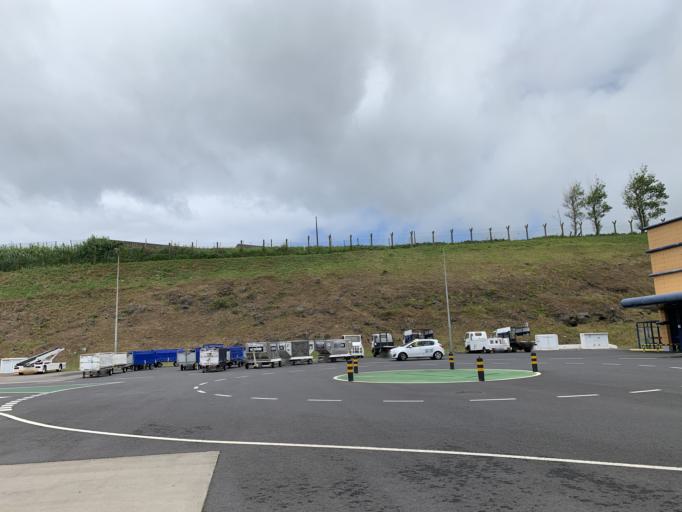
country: PT
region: Azores
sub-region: Ponta Delgada
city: Arrifes
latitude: 37.7493
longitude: -25.7121
